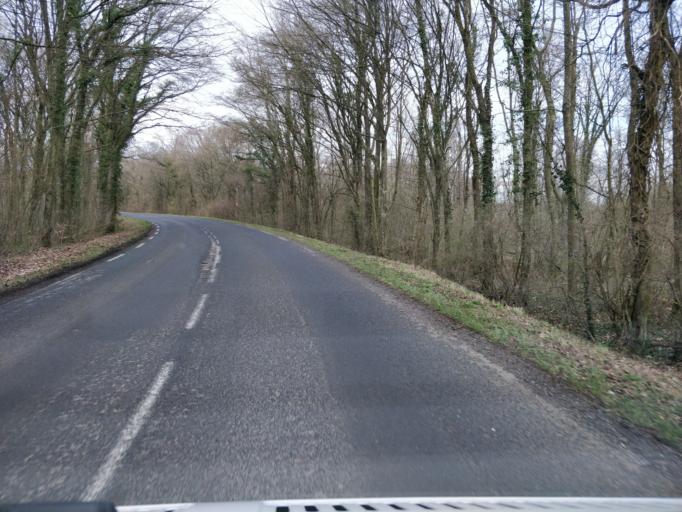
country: FR
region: Lorraine
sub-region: Departement de Meurthe-et-Moselle
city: Montauville
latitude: 48.9370
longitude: 5.8914
